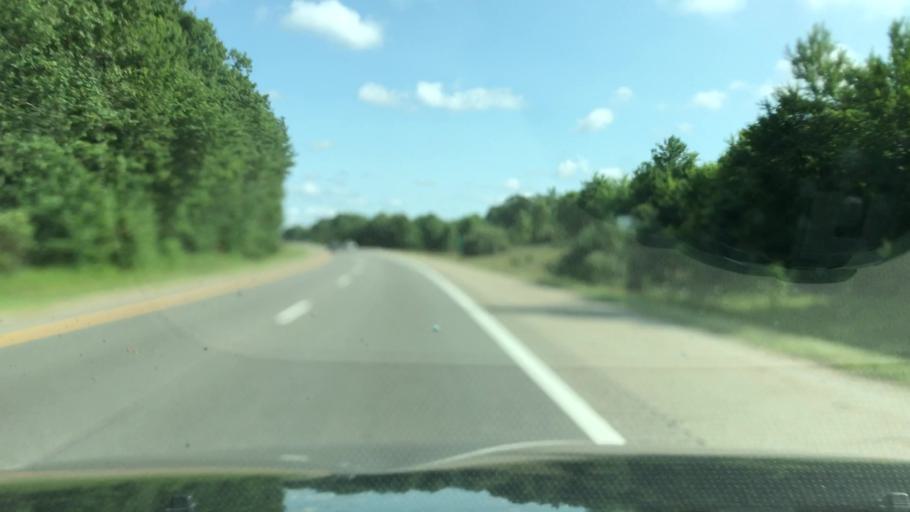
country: US
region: Michigan
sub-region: Kent County
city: Cedar Springs
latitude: 43.2381
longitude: -85.5615
